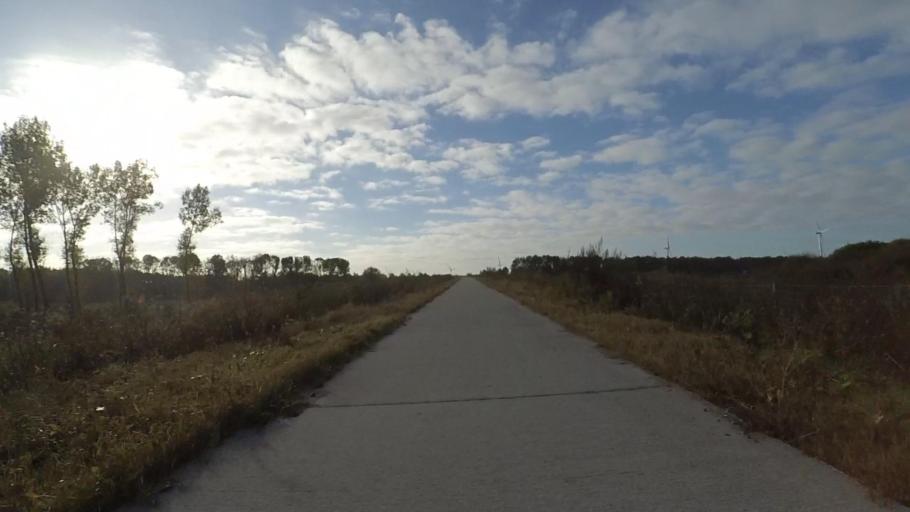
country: NL
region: Flevoland
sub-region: Gemeente Zeewolde
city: Zeewolde
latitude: 52.3269
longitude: 5.4492
